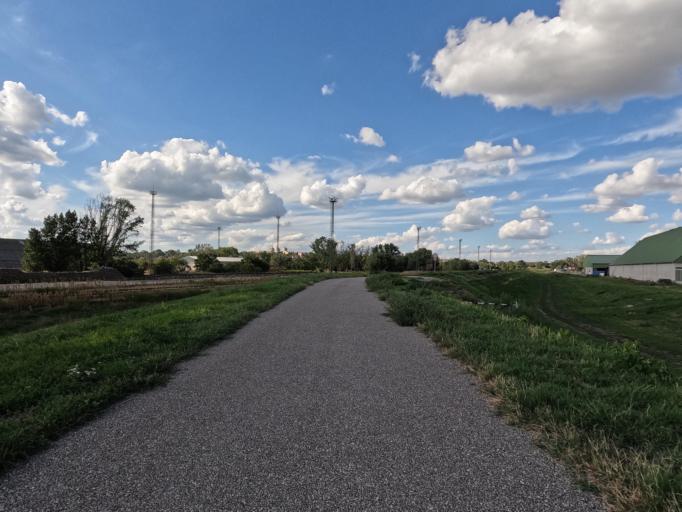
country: HU
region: Tolna
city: Paks
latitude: 46.6023
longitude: 18.8539
